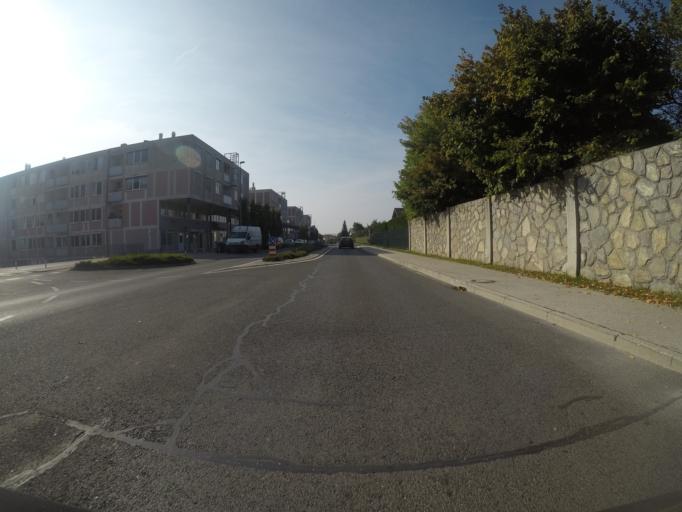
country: SI
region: Kamnik
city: Kamnik
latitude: 46.2186
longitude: 14.6043
